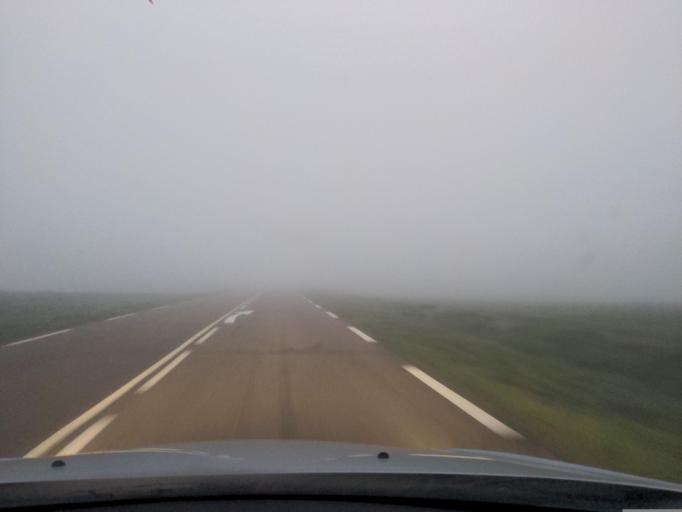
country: FR
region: Champagne-Ardenne
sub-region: Departement de la Haute-Marne
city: Langres
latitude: 47.7981
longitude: 5.2424
